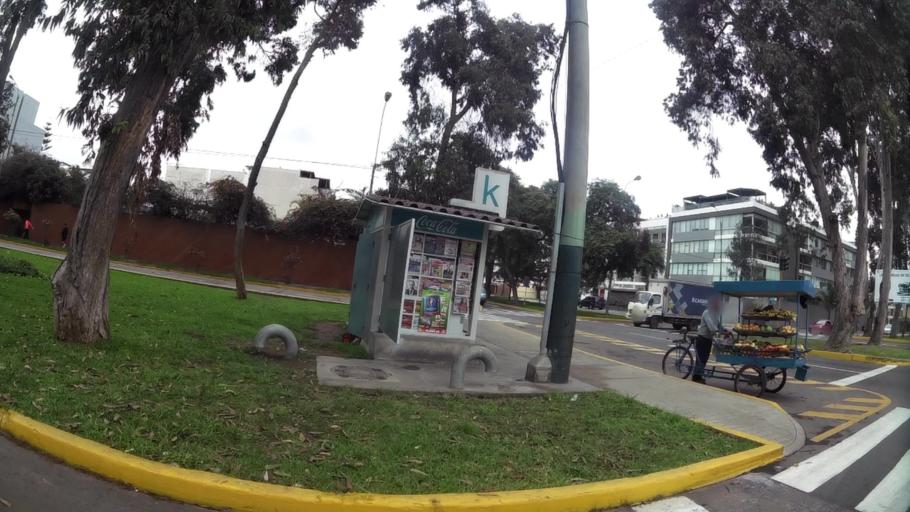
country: PE
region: Lima
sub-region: Lima
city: San Luis
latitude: -12.1078
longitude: -76.9846
